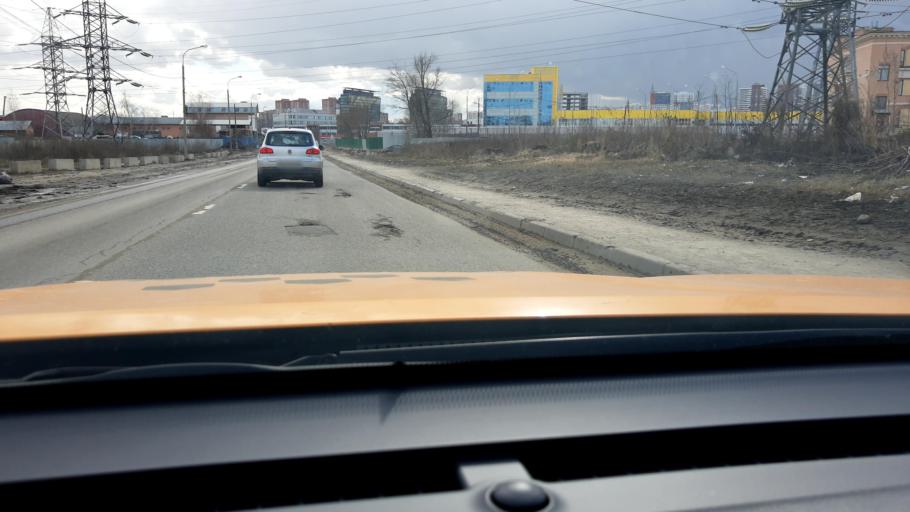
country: RU
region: Moscow
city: Khimki
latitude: 55.9161
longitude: 37.4216
